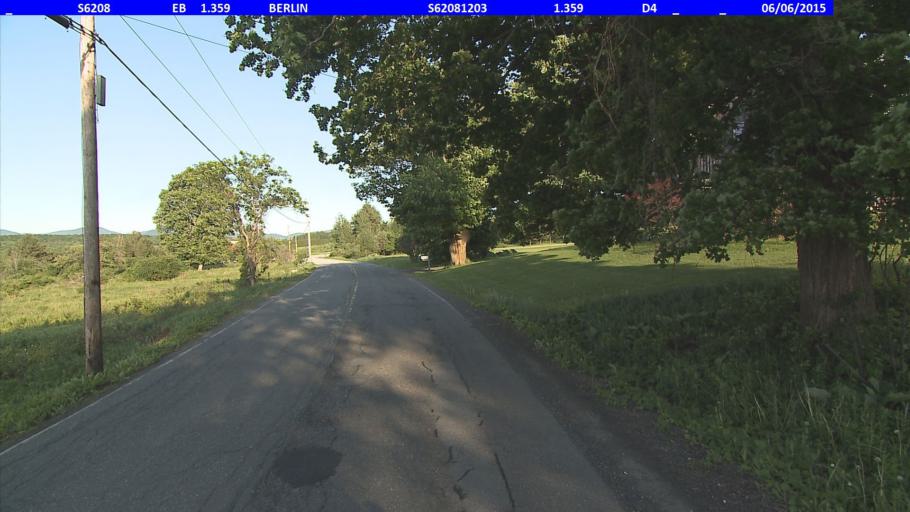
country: US
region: Vermont
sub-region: Washington County
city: South Barre
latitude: 44.1961
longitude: -72.5652
